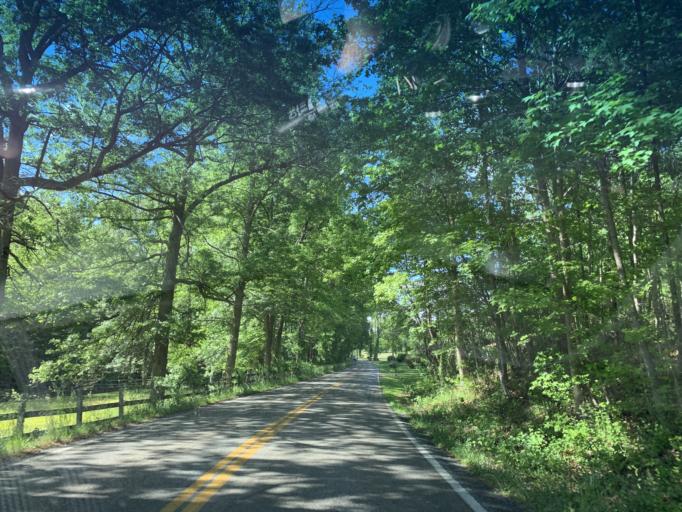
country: US
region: Maryland
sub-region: Cecil County
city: North East
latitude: 39.5430
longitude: -75.9177
